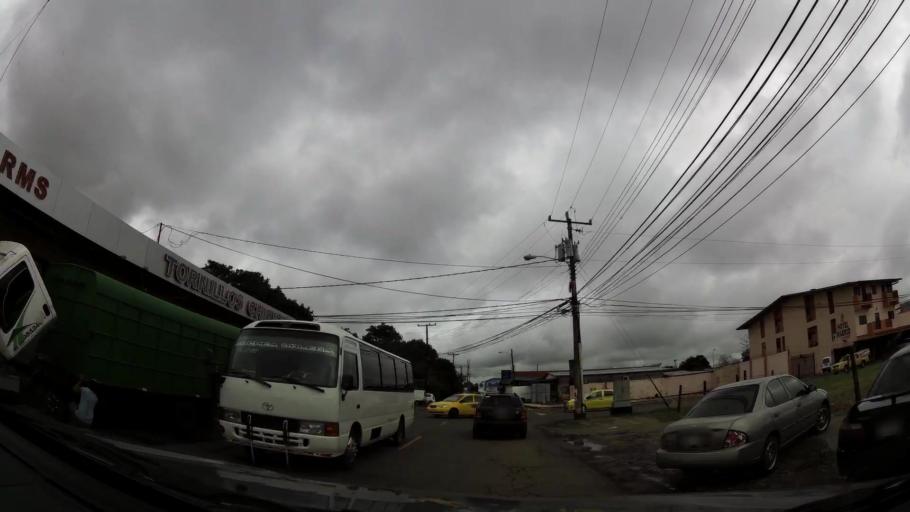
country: PA
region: Chiriqui
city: David
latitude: 8.4342
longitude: -82.4253
